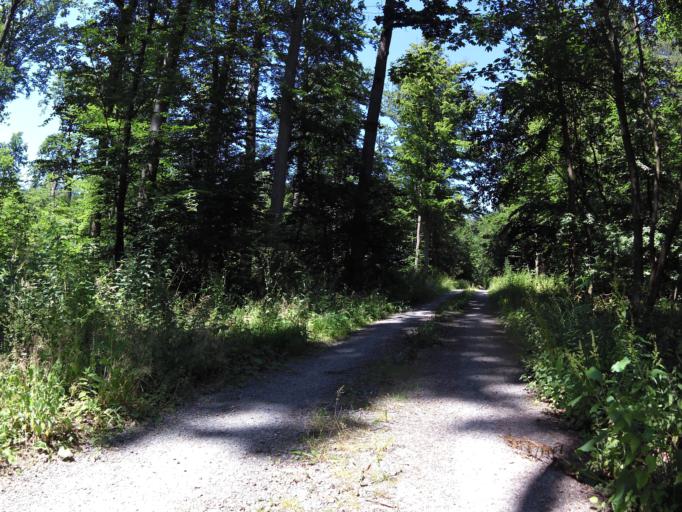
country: DE
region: Bavaria
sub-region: Regierungsbezirk Unterfranken
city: Reichenberg
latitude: 49.7238
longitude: 9.8779
